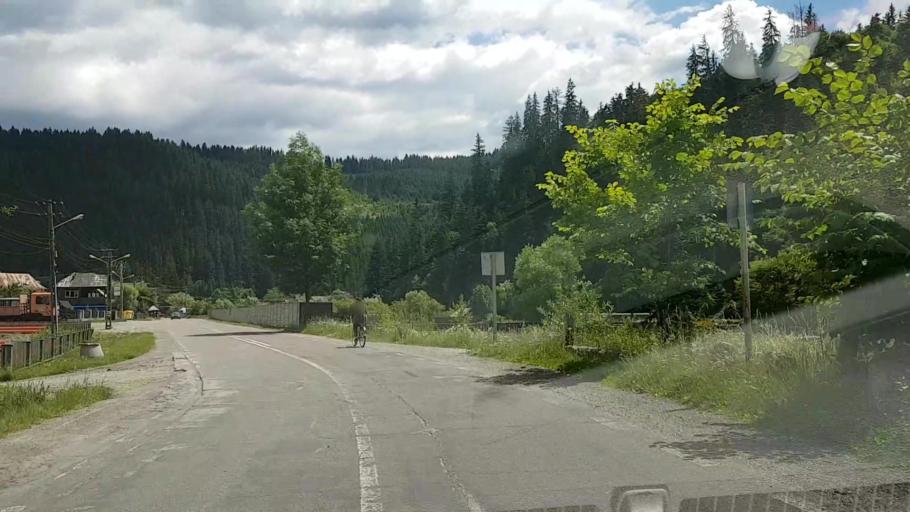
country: RO
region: Suceava
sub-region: Comuna Brosteni
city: Brosteni
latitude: 47.2386
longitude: 25.6921
